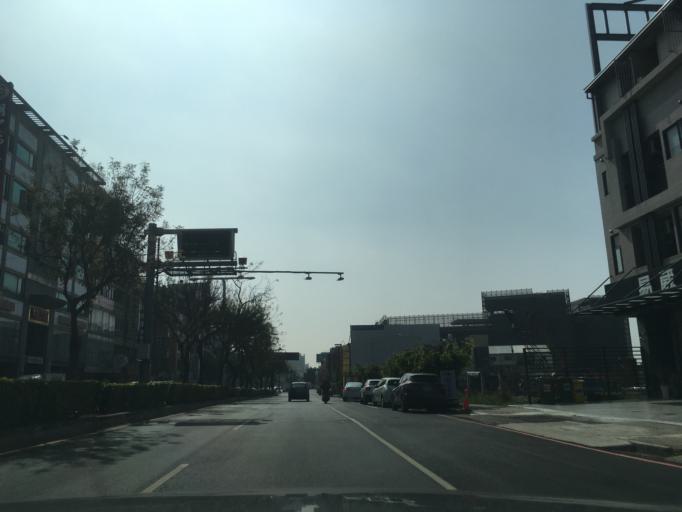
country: TW
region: Taiwan
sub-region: Taichung City
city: Taichung
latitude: 24.1948
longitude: 120.6586
